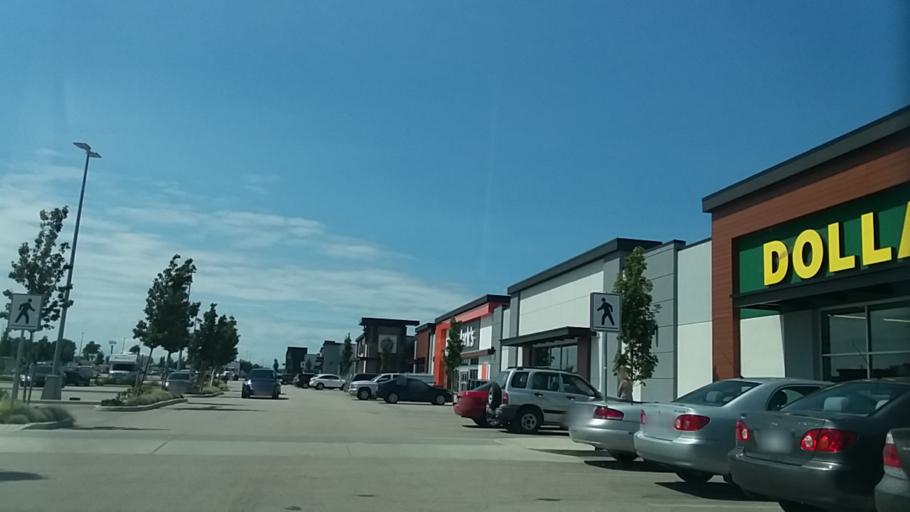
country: CA
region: British Columbia
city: Ladner
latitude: 49.0424
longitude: -123.0840
